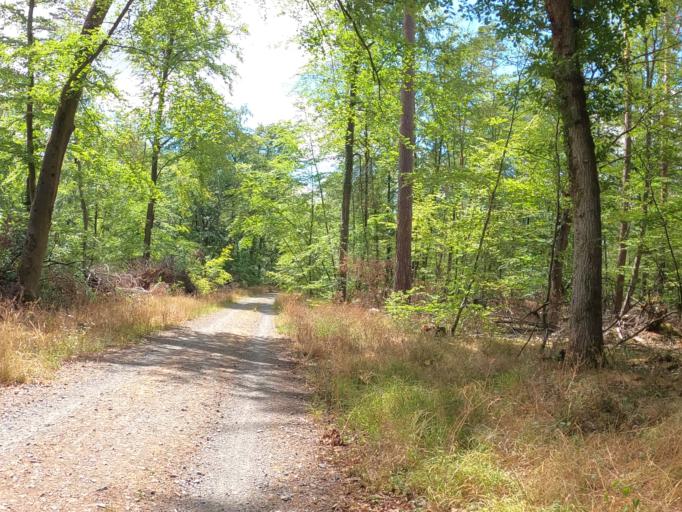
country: DE
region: Hesse
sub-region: Regierungsbezirk Darmstadt
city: Nauheim
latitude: 49.9765
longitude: 8.4921
